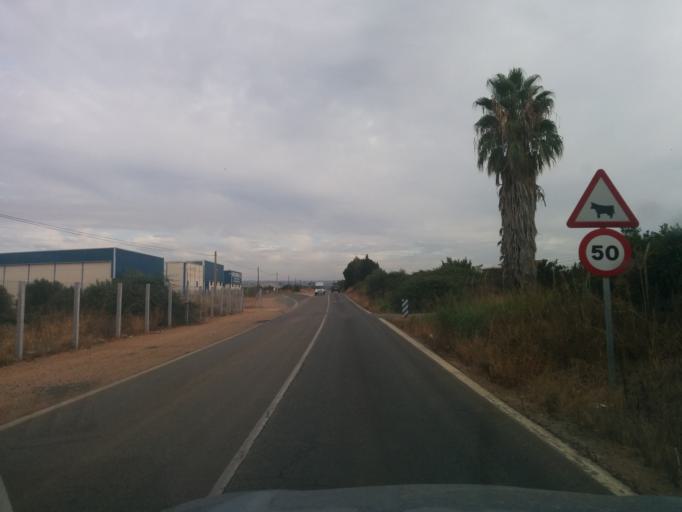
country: ES
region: Andalusia
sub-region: Provincia de Sevilla
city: Guillena
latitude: 37.5164
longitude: -6.0282
